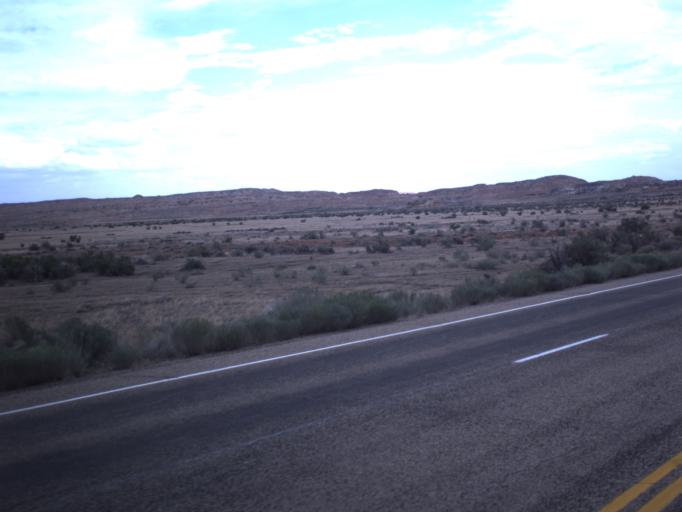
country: US
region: Utah
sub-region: Uintah County
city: Naples
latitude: 40.1361
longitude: -109.2687
